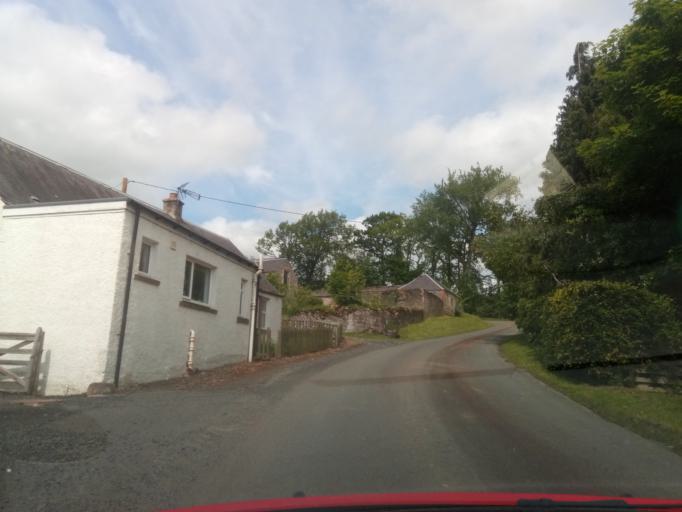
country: GB
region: Scotland
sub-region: The Scottish Borders
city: Selkirk
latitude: 55.5134
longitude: -2.7878
